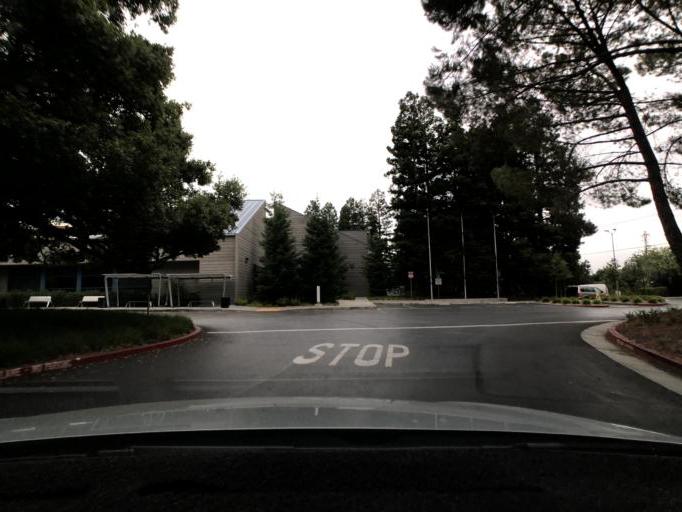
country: US
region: California
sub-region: Santa Clara County
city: Cupertino
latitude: 37.3170
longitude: -122.0511
